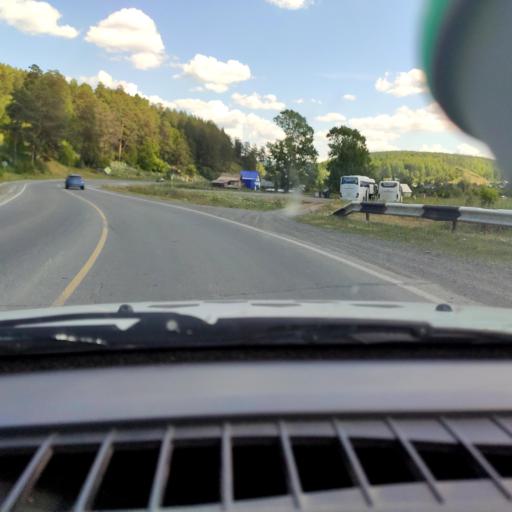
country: RU
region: Chelyabinsk
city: Mezhevoy
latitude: 55.1592
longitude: 58.8120
